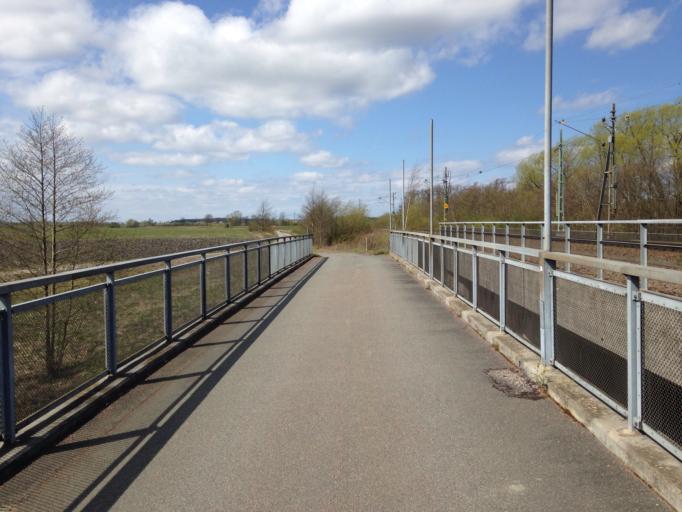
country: SE
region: Skane
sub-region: Kristianstads Kommun
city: Kristianstad
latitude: 56.0390
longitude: 14.1439
